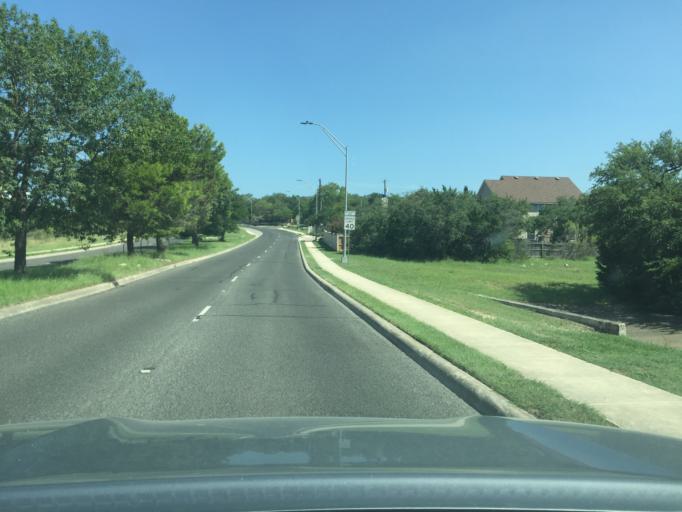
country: US
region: Texas
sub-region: Bexar County
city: Timberwood Park
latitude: 29.6586
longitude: -98.4970
